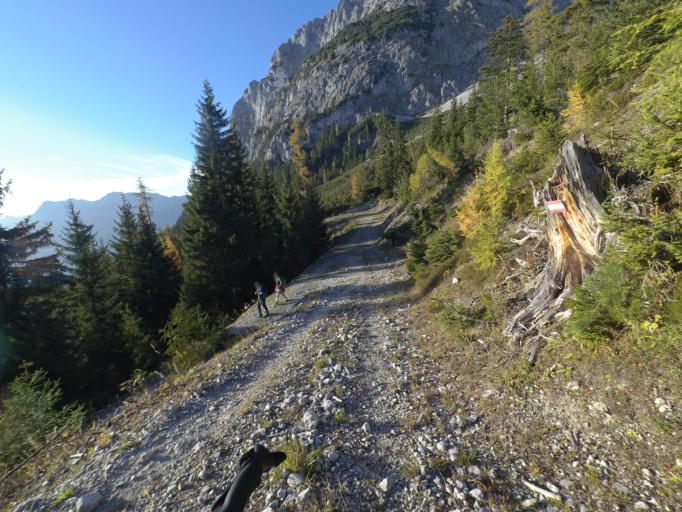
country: AT
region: Salzburg
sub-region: Politischer Bezirk Sankt Johann im Pongau
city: Werfenweng
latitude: 47.4867
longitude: 13.2295
